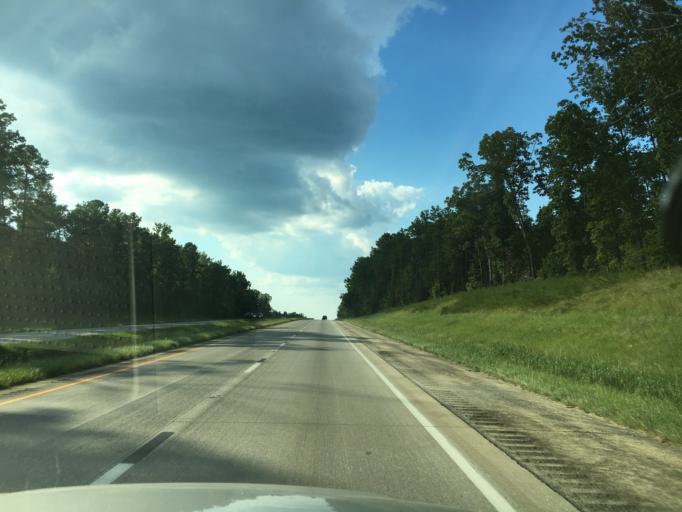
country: US
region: South Carolina
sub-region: Laurens County
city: Watts Mills
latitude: 34.5808
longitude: -82.0415
